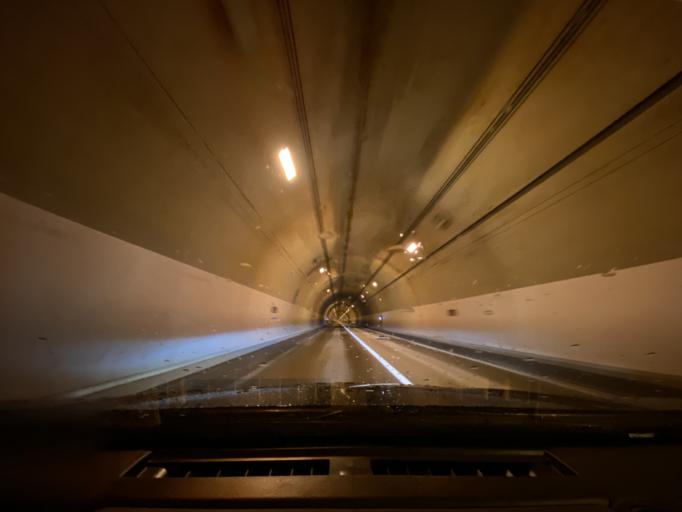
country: JP
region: Hokkaido
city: Rumoi
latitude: 43.6875
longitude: 141.3407
